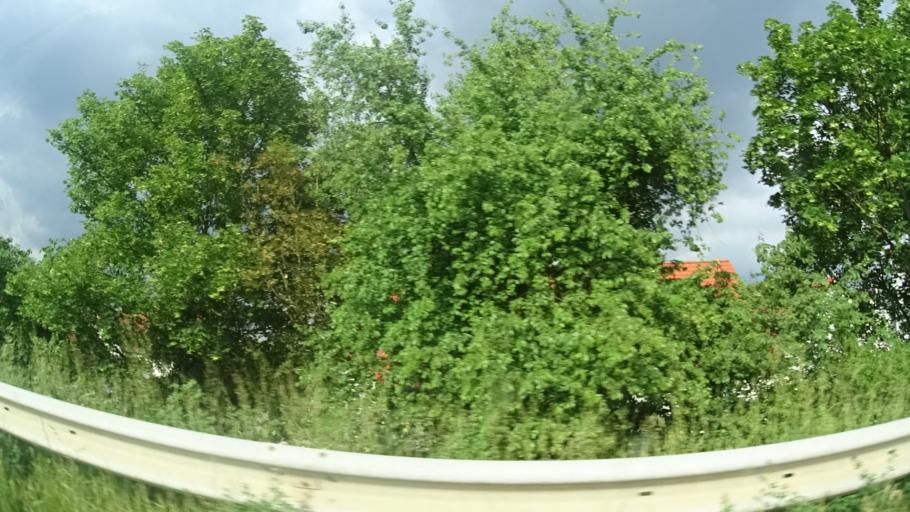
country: DE
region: Rheinland-Pfalz
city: Schifferstadt
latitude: 49.3897
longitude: 8.3652
